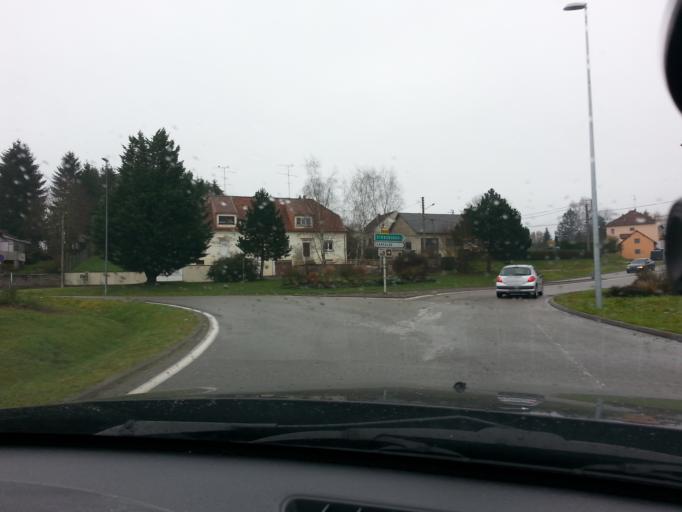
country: FR
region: Lorraine
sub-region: Departement de la Moselle
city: Farschviller
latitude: 49.0580
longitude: 6.9212
